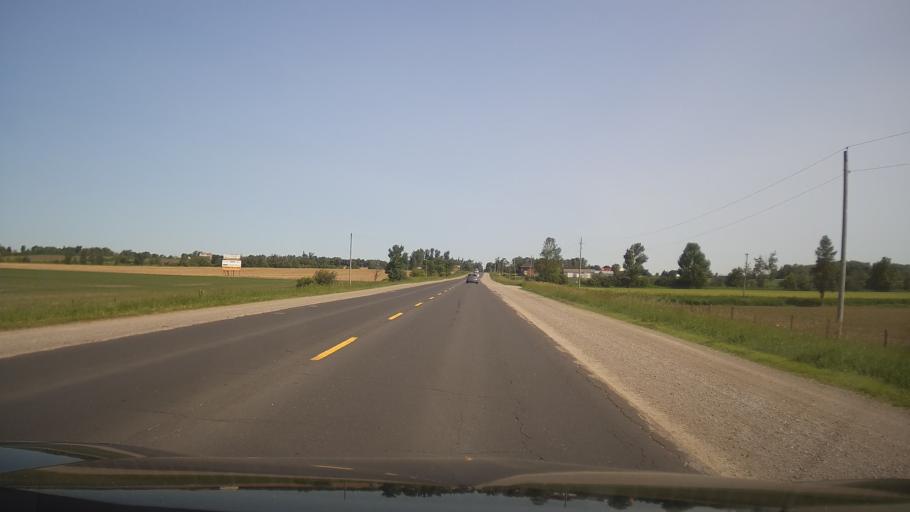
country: CA
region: Ontario
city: Omemee
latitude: 44.3240
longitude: -78.6844
